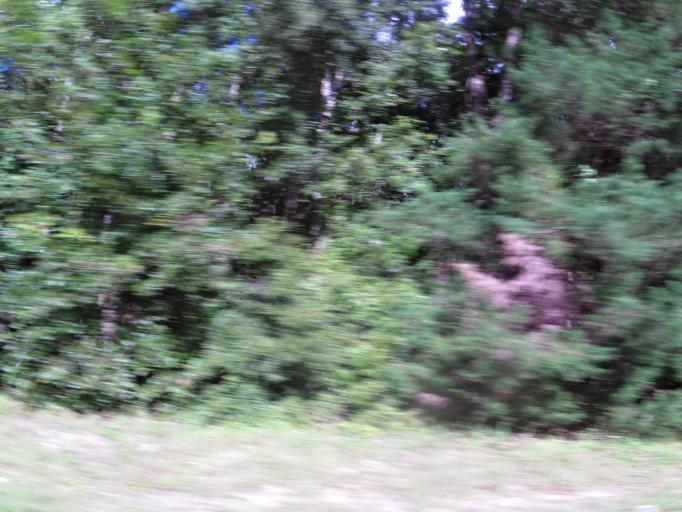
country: US
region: Georgia
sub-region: Camden County
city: Kingsland
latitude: 30.8305
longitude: -81.6963
